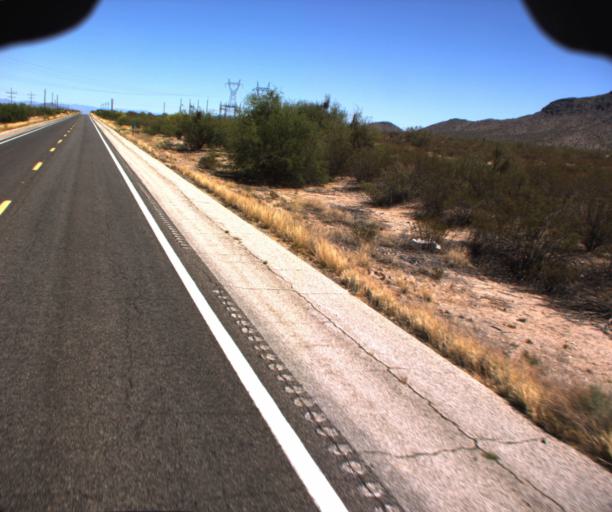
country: US
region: Arizona
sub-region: La Paz County
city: Salome
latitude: 33.9048
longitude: -113.2931
